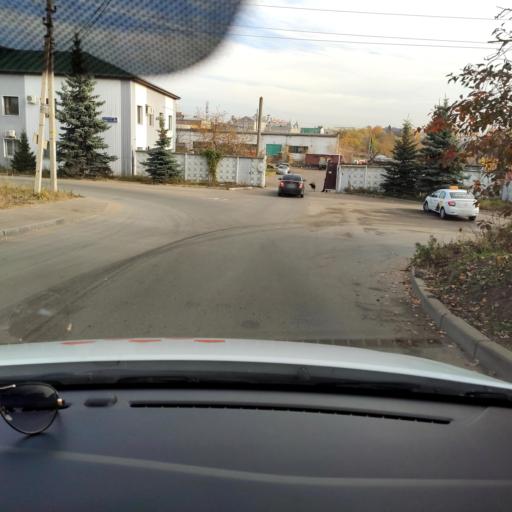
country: RU
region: Tatarstan
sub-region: Gorod Kazan'
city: Kazan
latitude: 55.8066
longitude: 49.0627
